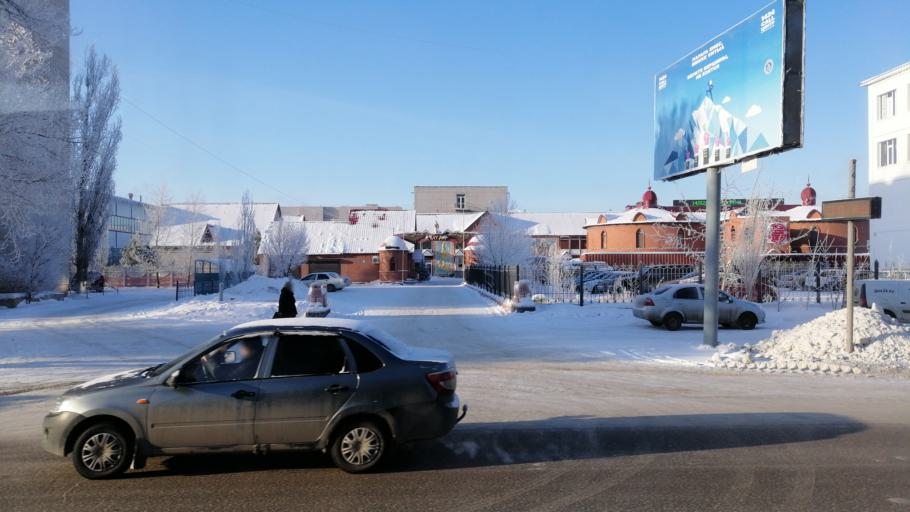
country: KZ
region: Aqtoebe
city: Aqtobe
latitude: 50.2939
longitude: 57.1484
